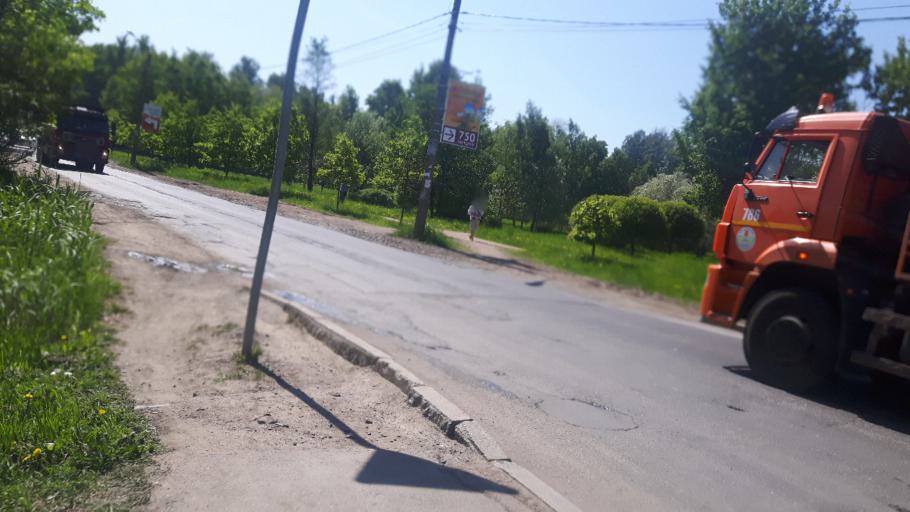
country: RU
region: St.-Petersburg
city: Sosnovaya Polyana
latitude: 59.8497
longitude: 30.1208
